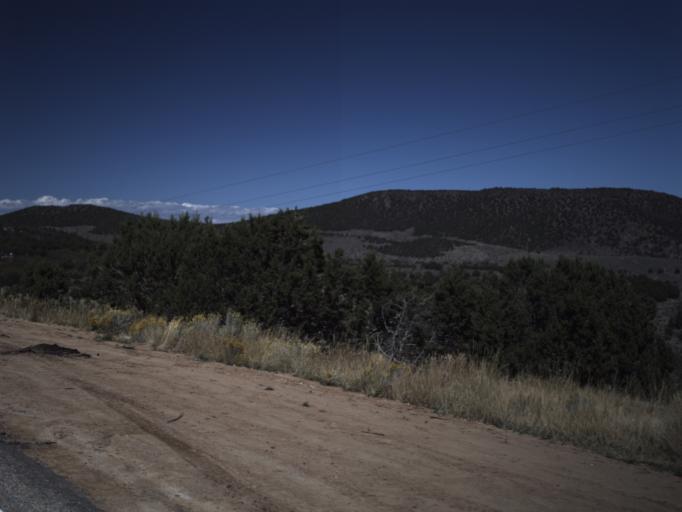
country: US
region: Utah
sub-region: Washington County
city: Enterprise
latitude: 37.5220
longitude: -113.6392
